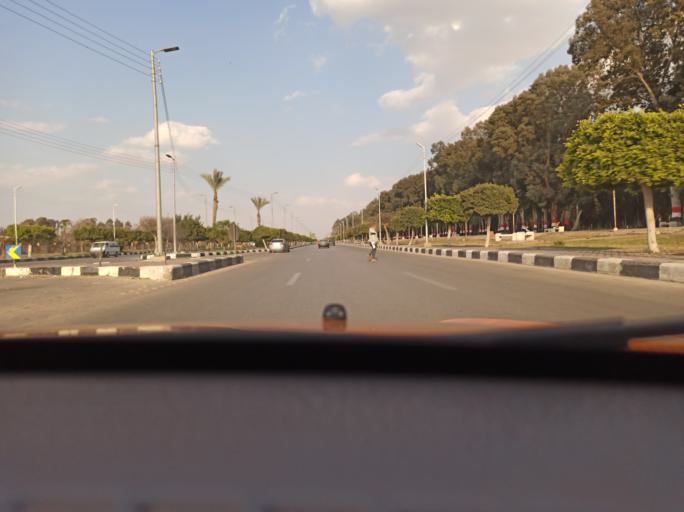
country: EG
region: Al Isma'iliyah
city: Ismailia
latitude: 30.6170
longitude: 32.2632
